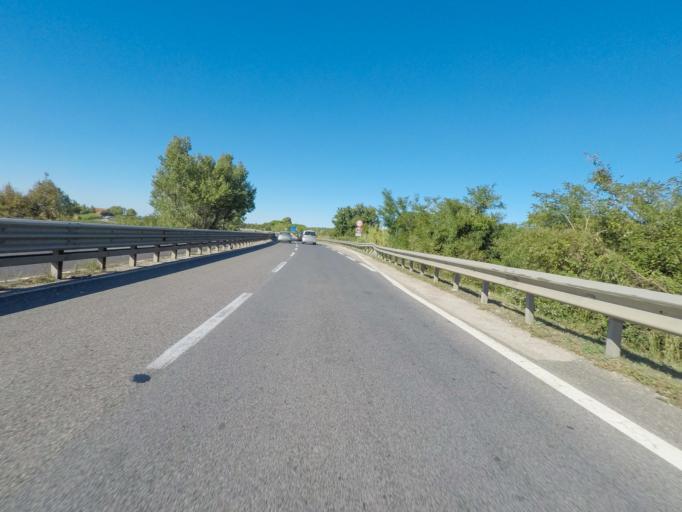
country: IT
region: Tuscany
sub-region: Provincia di Grosseto
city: Grosseto
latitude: 42.7131
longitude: 11.1446
